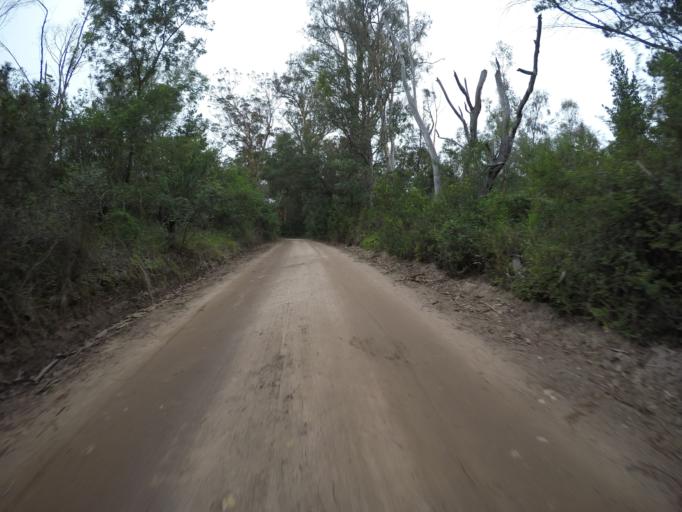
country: ZA
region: Western Cape
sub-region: Eden District Municipality
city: Knysna
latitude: -34.0056
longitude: 22.7951
